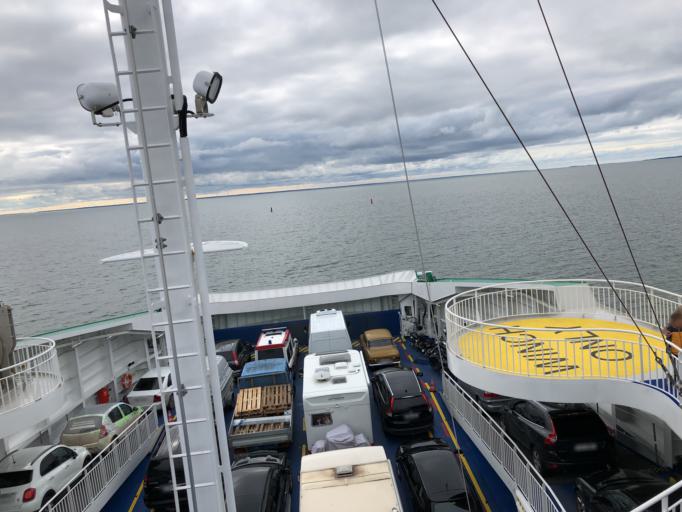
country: EE
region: Laeaene
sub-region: Vormsi vald
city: Hullo
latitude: 58.9079
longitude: 23.3597
